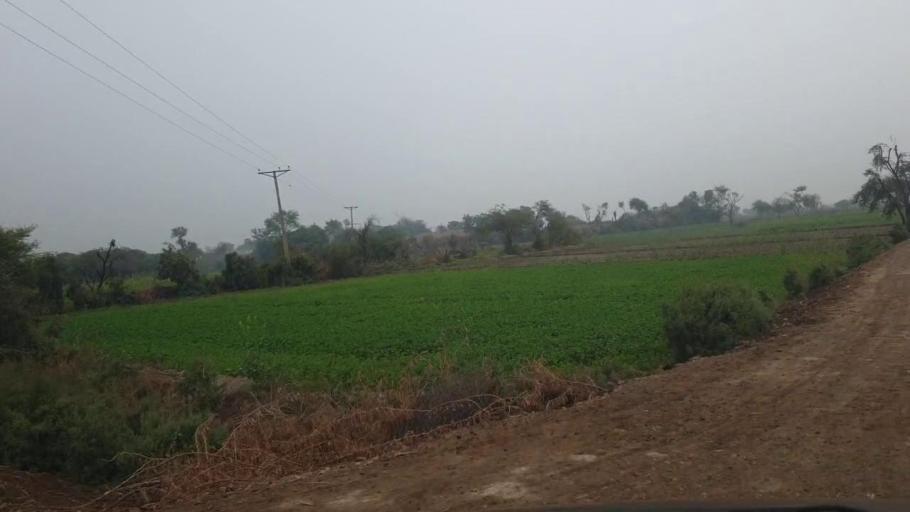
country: PK
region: Sindh
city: Tando Adam
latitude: 25.8361
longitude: 68.6827
